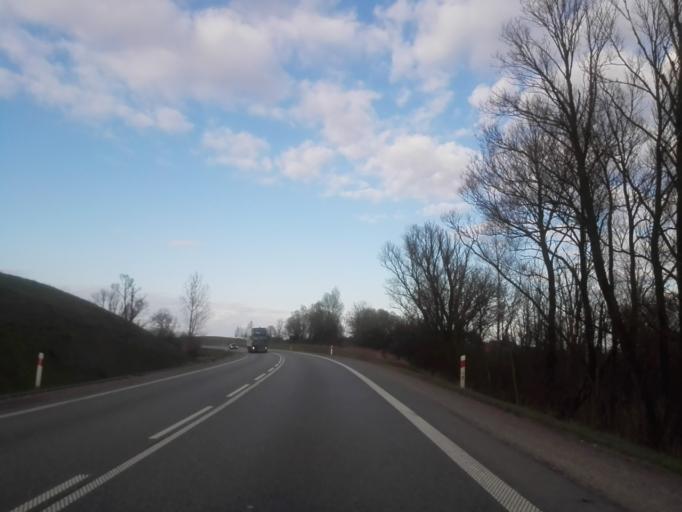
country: PL
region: Podlasie
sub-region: Suwalki
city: Suwalki
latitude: 54.1969
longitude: 23.0174
